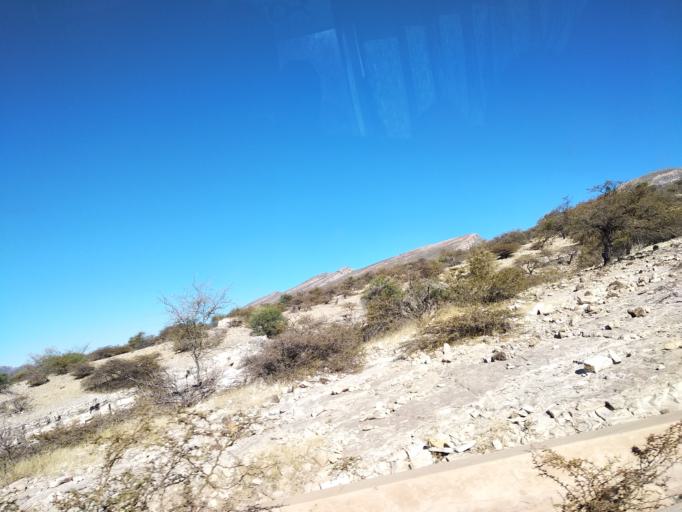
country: BO
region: Cochabamba
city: Mizque
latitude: -18.0819
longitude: -65.7462
